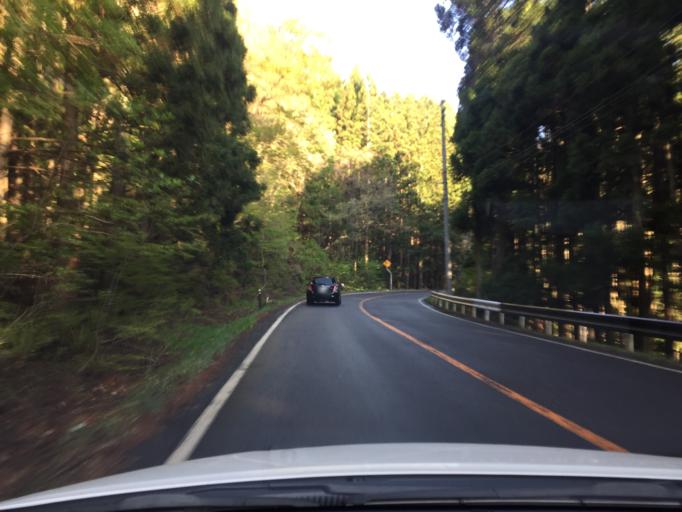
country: JP
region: Fukushima
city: Inawashiro
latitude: 37.6189
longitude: 140.1157
